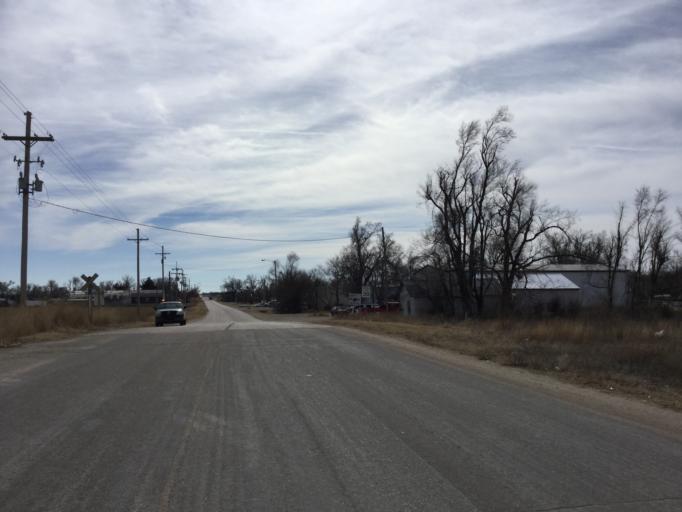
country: US
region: Kansas
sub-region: Rice County
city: Lyons
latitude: 38.3520
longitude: -98.3494
